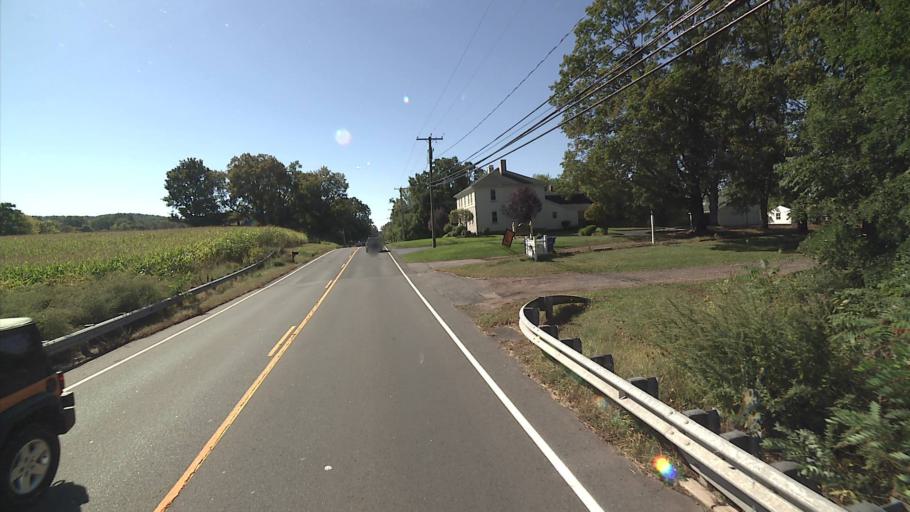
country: US
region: Connecticut
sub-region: Tolland County
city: Ellington
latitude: 41.9145
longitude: -72.4538
